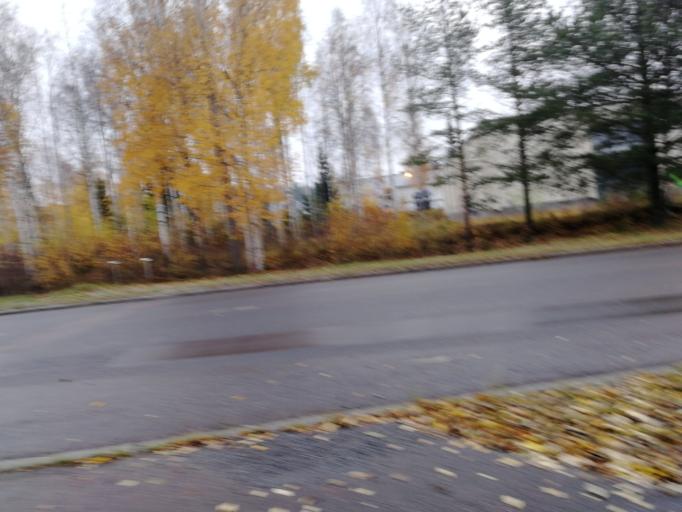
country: FI
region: Pirkanmaa
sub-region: Tampere
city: Tampere
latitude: 61.4531
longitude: 23.8842
